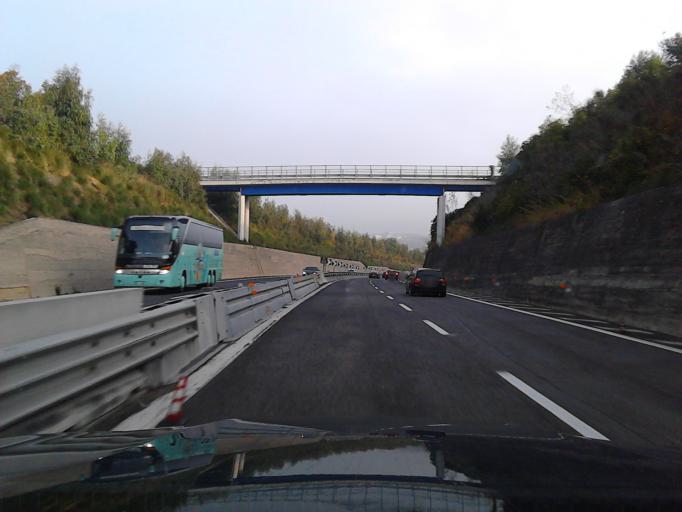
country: IT
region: Abruzzo
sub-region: Provincia di Chieti
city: San Vito Chietino
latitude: 42.2991
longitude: 14.4290
